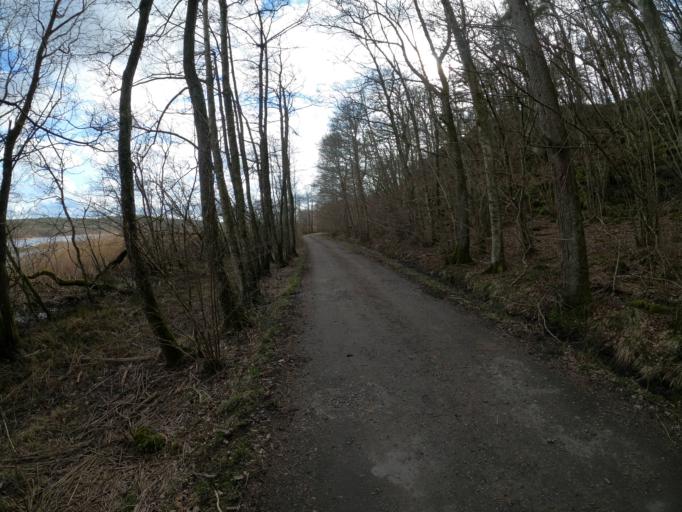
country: SE
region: Vaestra Goetaland
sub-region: Harryda Kommun
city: Molnlycke
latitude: 57.6324
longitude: 12.0974
